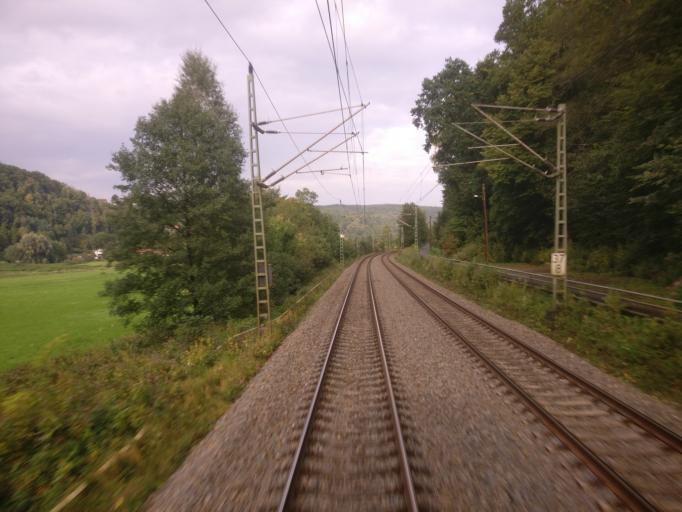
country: DE
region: Saxony
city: Stadt Wehlen
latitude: 50.9511
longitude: 14.0225
